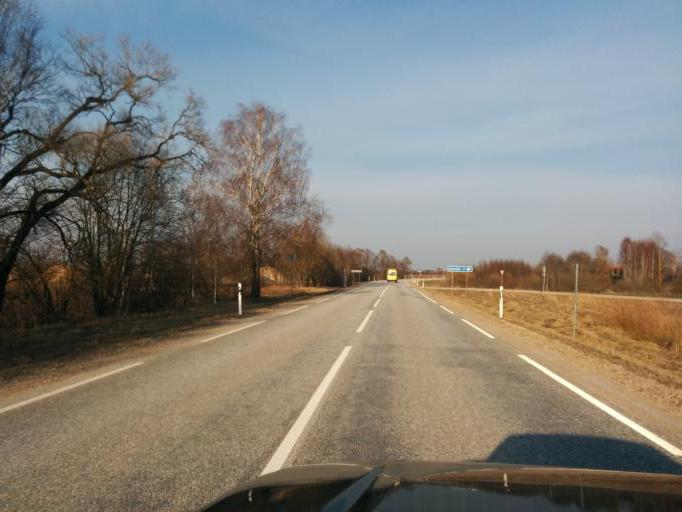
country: LV
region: Lecava
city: Iecava
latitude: 56.5909
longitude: 24.1636
